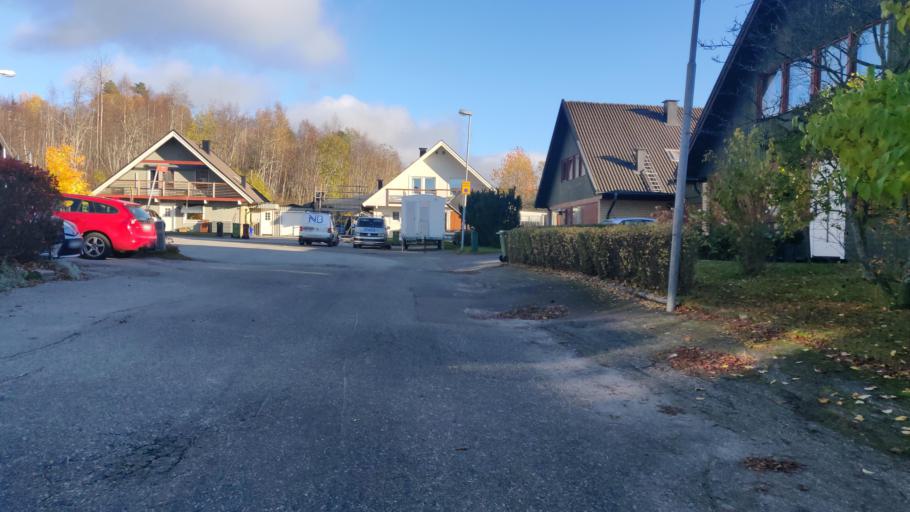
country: SE
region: Vaesternorrland
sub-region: Sundsvalls Kommun
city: Nolby
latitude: 62.2755
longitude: 17.3629
